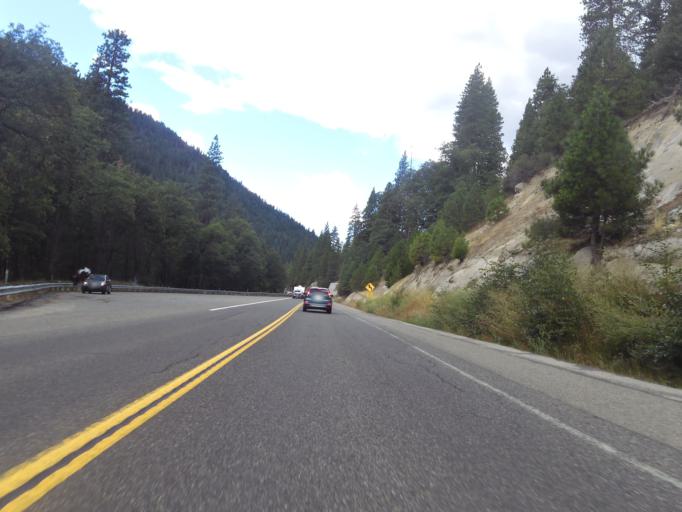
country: US
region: California
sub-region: El Dorado County
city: South Lake Tahoe
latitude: 38.7779
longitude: -120.2605
